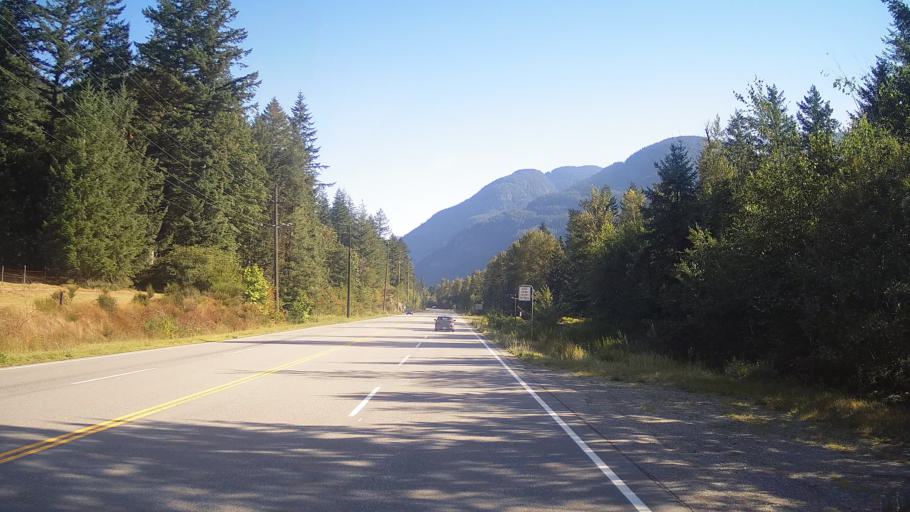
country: CA
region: British Columbia
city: Hope
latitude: 49.4801
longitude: -121.4233
